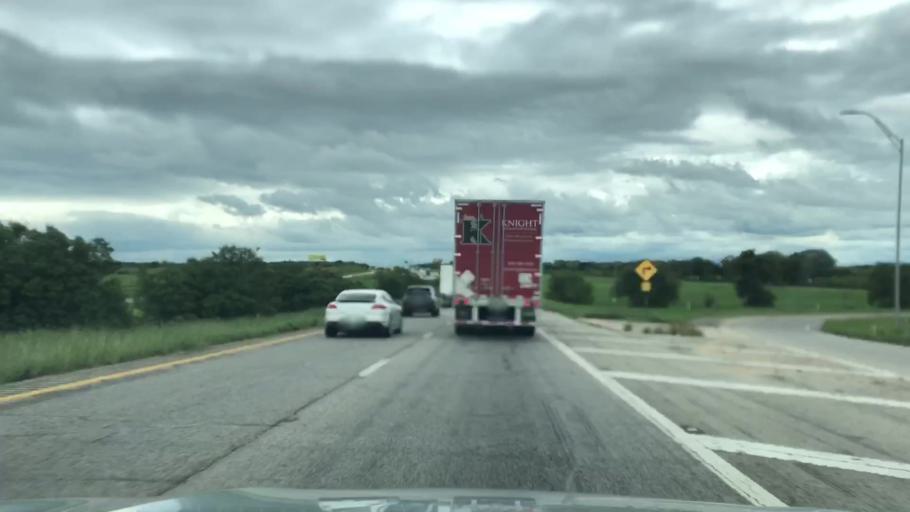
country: US
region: Texas
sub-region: Guadalupe County
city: Seguin
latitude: 29.5990
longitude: -97.9231
